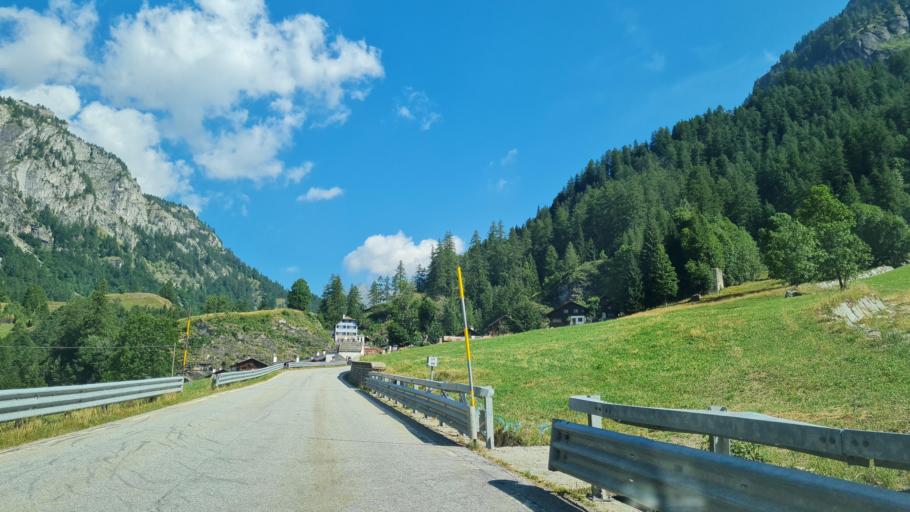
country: IT
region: Piedmont
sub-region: Provincia Verbano-Cusio-Ossola
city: Formazza
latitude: 46.3850
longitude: 8.4250
